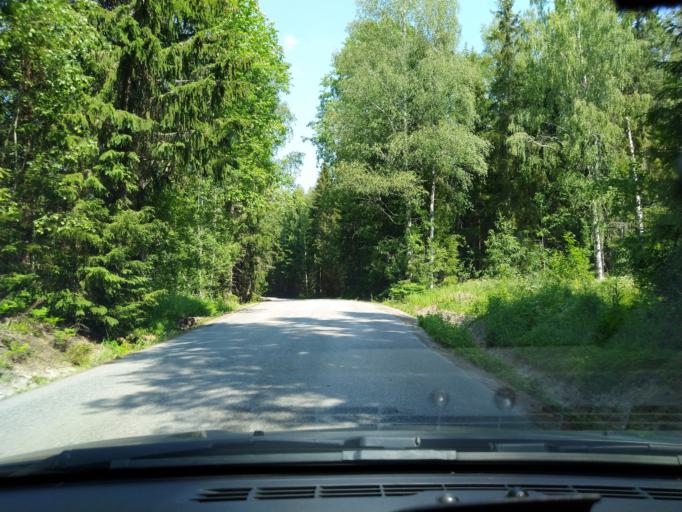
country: FI
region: Uusimaa
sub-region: Helsinki
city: Lohja
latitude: 60.3527
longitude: 24.0892
